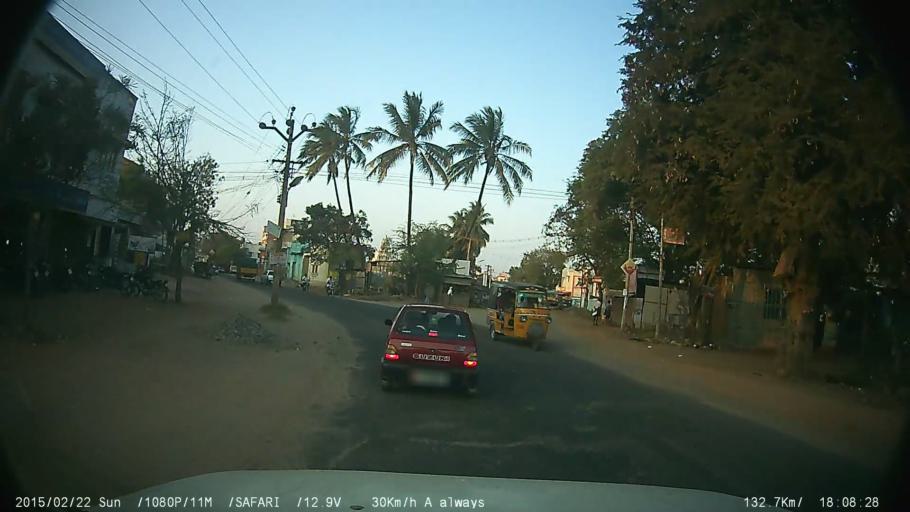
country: IN
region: Tamil Nadu
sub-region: Theni
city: Chinnamanur
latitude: 9.8373
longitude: 77.3793
